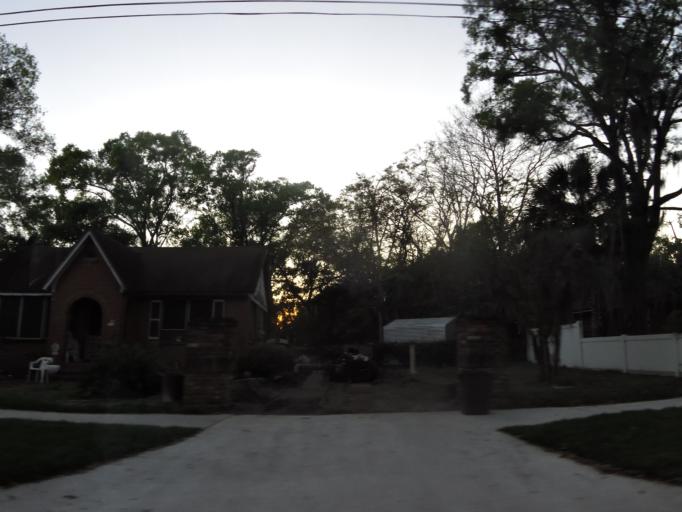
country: US
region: Florida
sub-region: Duval County
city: Jacksonville
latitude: 30.3305
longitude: -81.7165
